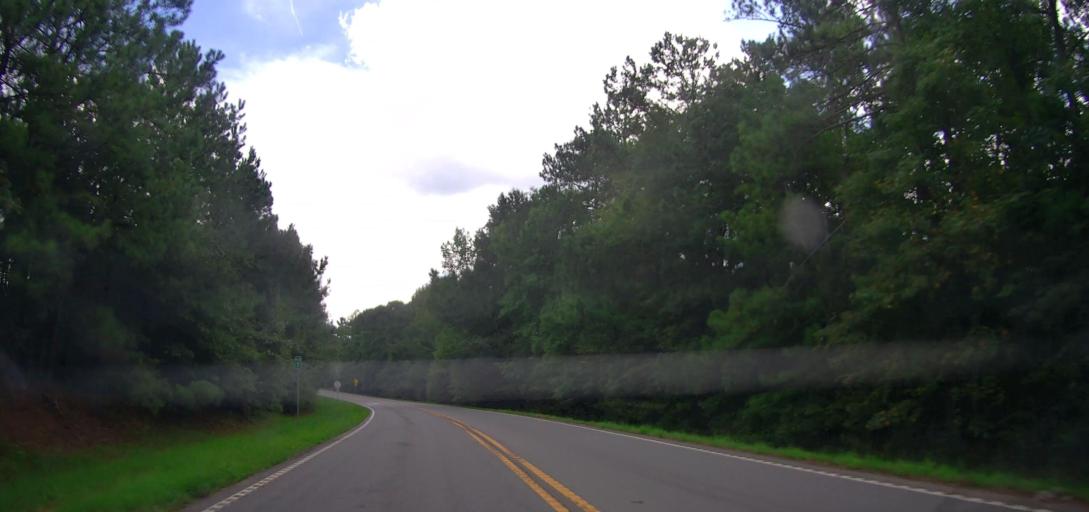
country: US
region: Georgia
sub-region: Talbot County
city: Talbotton
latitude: 32.6348
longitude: -84.4926
